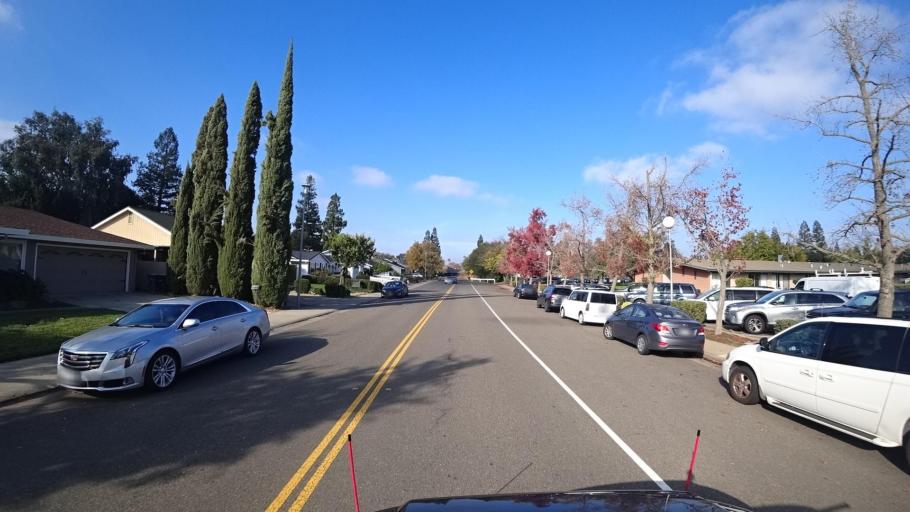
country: US
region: California
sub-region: Sacramento County
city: Elk Grove
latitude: 38.4129
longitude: -121.3606
